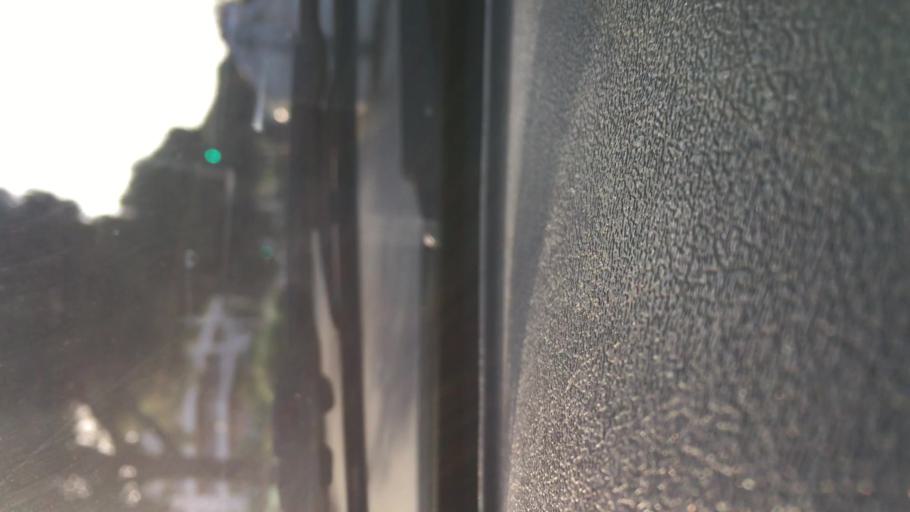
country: IT
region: Latium
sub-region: Citta metropolitana di Roma Capitale
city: Rome
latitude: 41.8337
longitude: 12.4977
